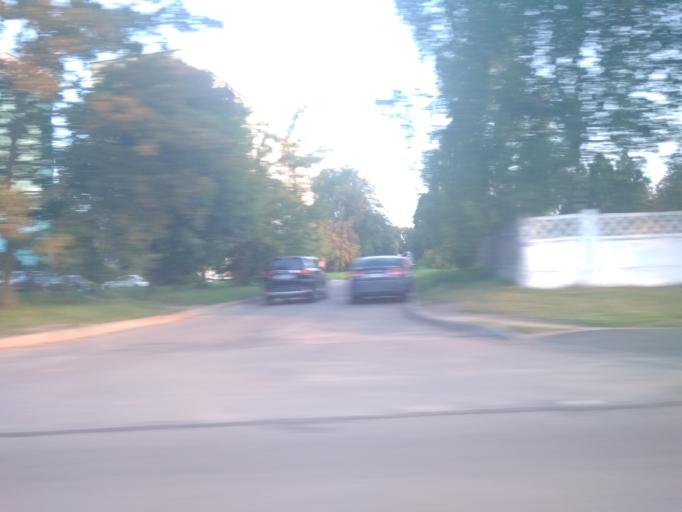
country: BY
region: Minsk
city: Zhdanovichy
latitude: 53.9305
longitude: 27.4685
